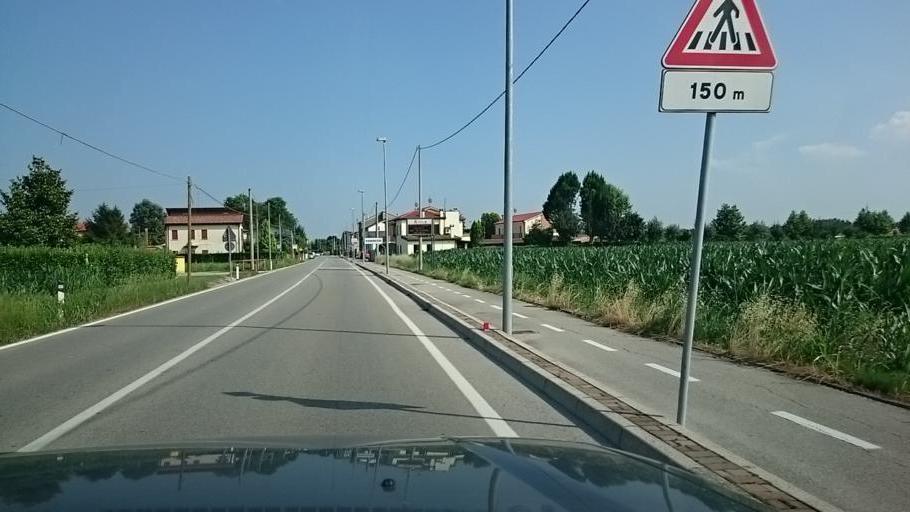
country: IT
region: Veneto
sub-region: Provincia di Padova
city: Saletto
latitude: 45.4650
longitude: 11.8696
